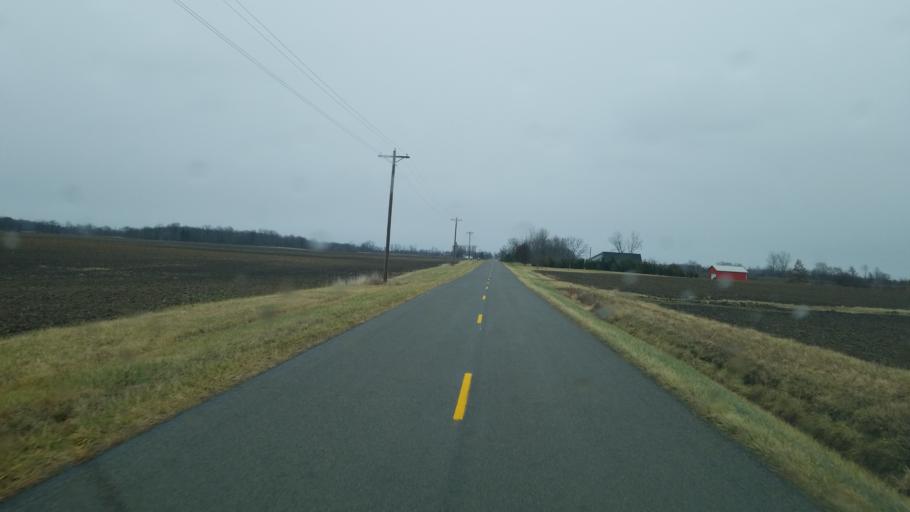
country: US
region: Ohio
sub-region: Logan County
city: Northwood
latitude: 40.4513
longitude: -83.5755
